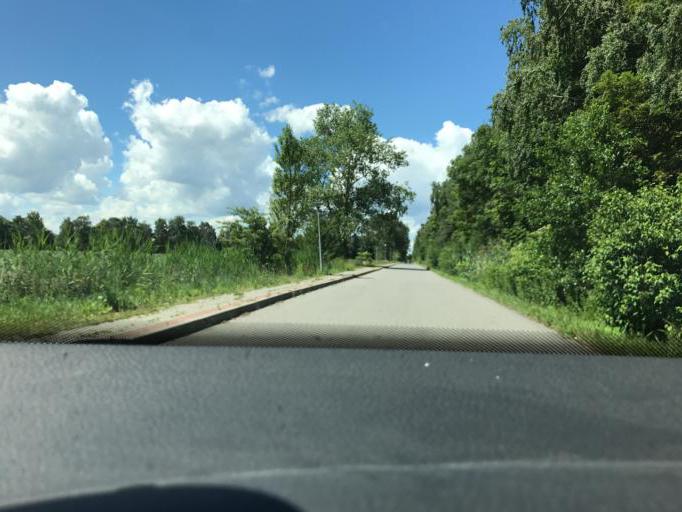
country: PL
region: Pomeranian Voivodeship
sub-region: Gdansk
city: Gdansk
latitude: 54.3272
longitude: 18.7374
